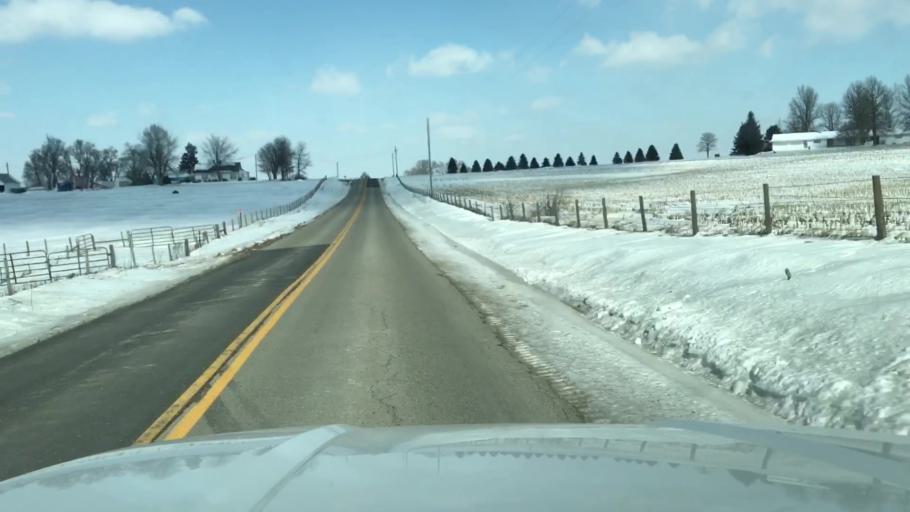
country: US
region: Missouri
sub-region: Nodaway County
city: Maryville
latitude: 40.3600
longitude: -94.7220
